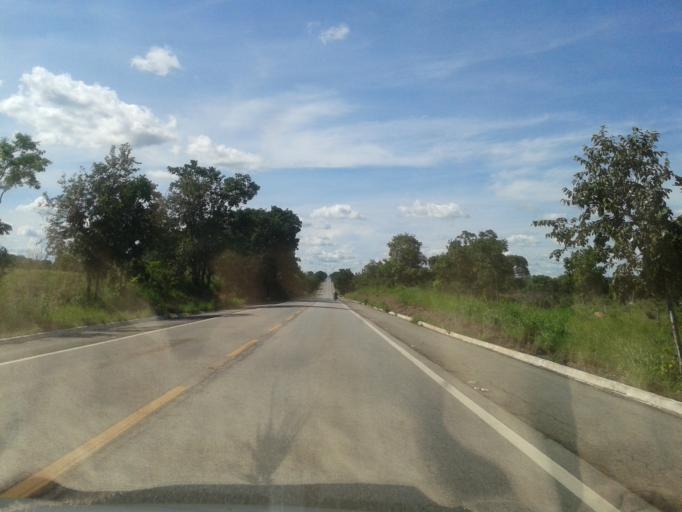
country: BR
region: Goias
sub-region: Mozarlandia
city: Mozarlandia
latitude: -15.2765
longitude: -50.4792
